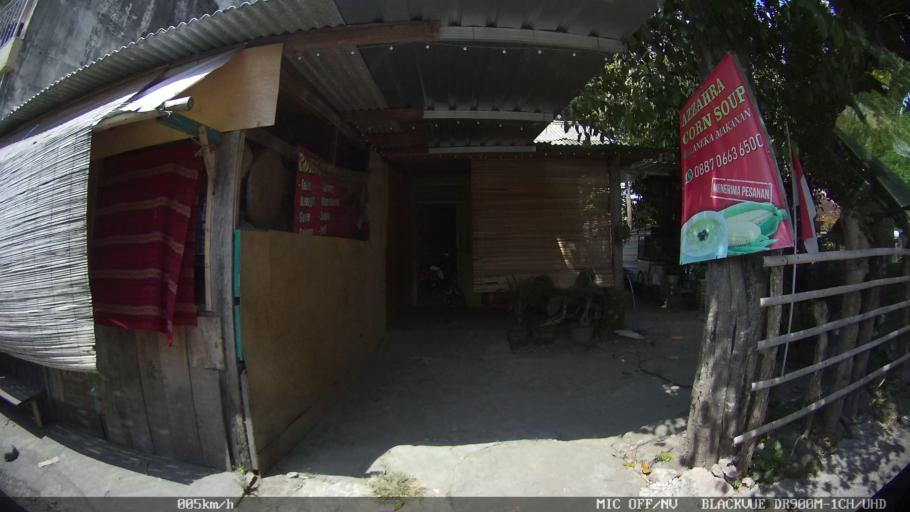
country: ID
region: Daerah Istimewa Yogyakarta
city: Sewon
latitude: -7.8305
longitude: 110.3880
